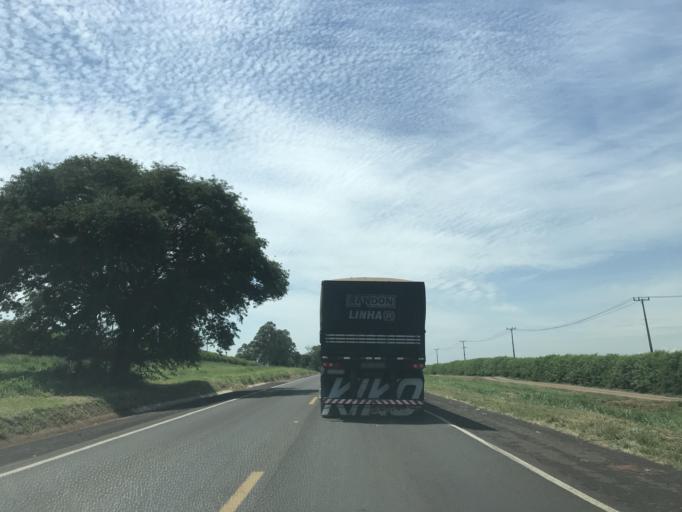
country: BR
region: Parana
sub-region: Paranavai
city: Nova Aurora
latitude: -22.9690
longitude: -52.6300
